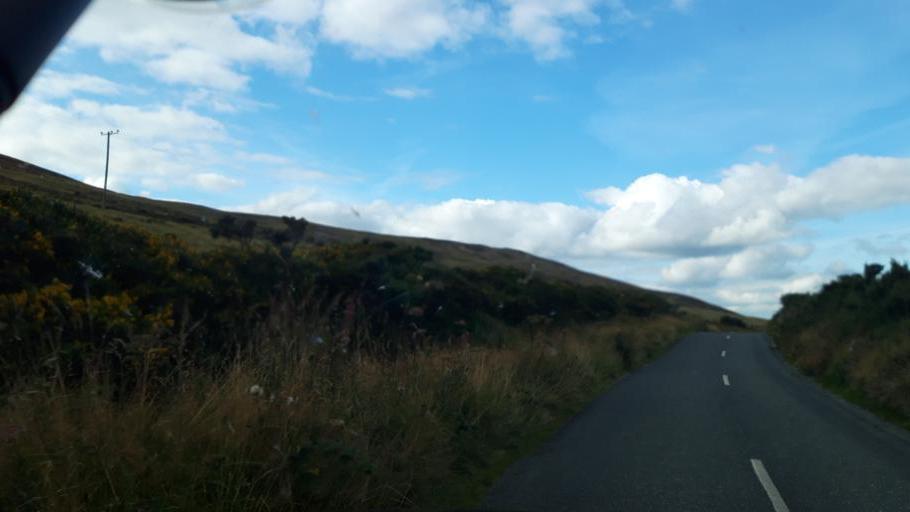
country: GB
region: Northern Ireland
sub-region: Down District
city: Warrenpoint
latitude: 54.0432
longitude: -6.2693
